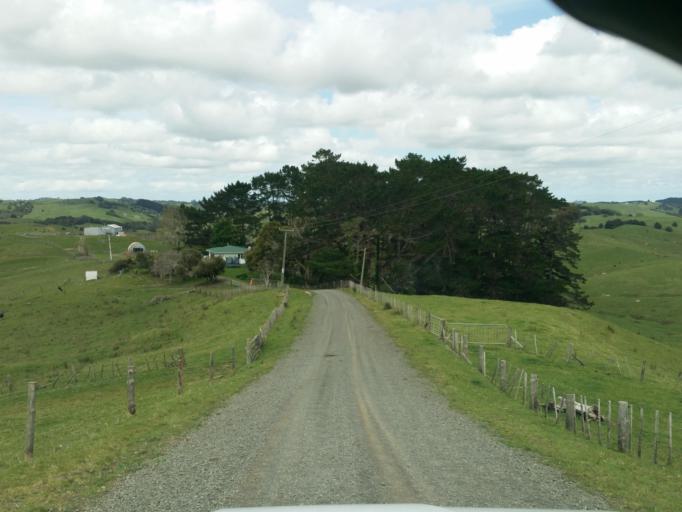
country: NZ
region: Northland
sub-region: Kaipara District
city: Dargaville
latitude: -35.9345
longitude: 174.0208
